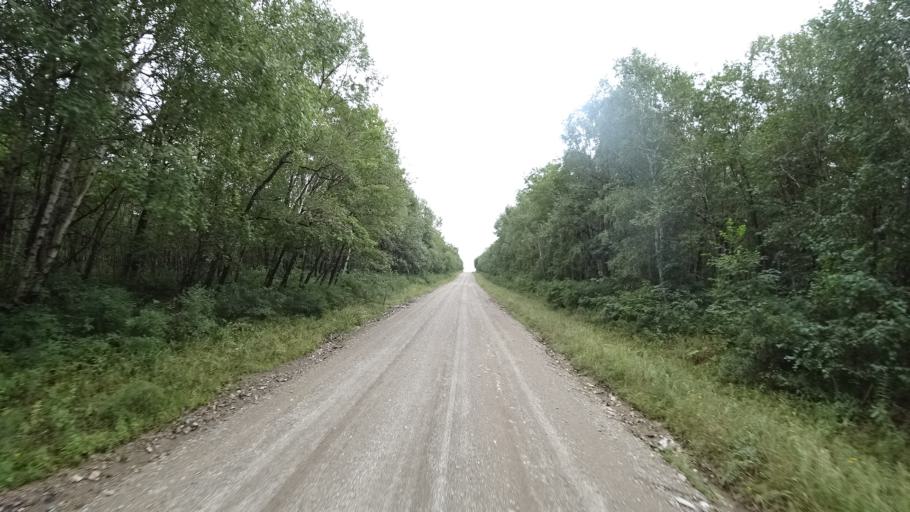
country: RU
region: Primorskiy
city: Ivanovka
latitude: 44.0384
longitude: 132.4978
